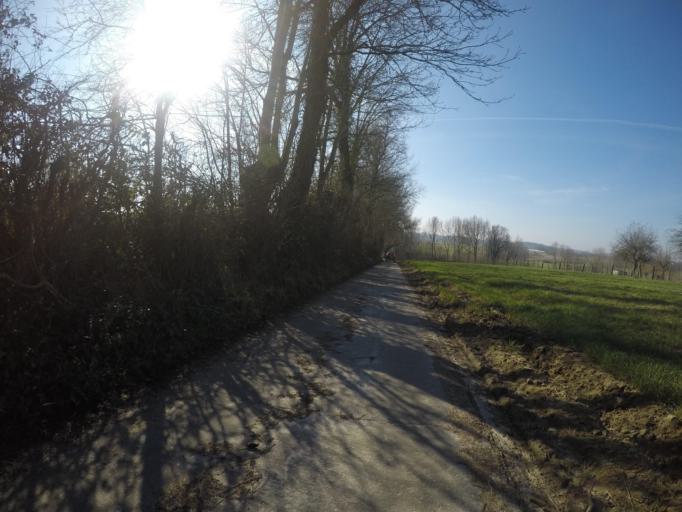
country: BE
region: Flanders
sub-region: Provincie Oost-Vlaanderen
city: Sint-Maria-Lierde
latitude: 50.8007
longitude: 3.7873
